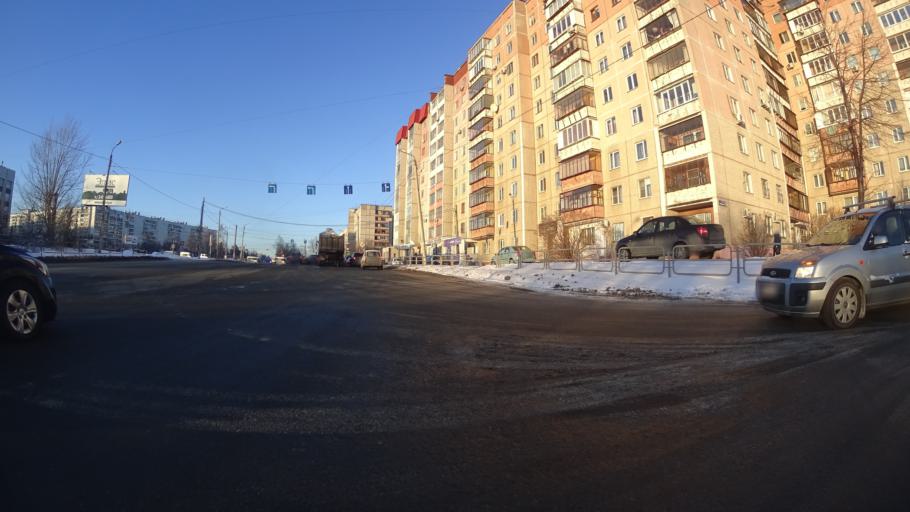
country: RU
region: Chelyabinsk
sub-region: Gorod Chelyabinsk
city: Chelyabinsk
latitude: 55.1905
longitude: 61.3635
